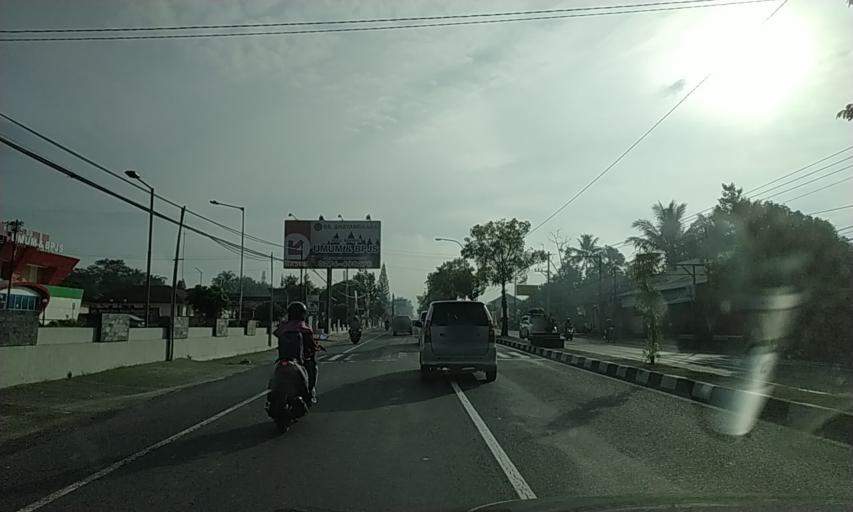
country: ID
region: Central Java
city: Candi Prambanan
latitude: -7.7667
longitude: 110.4718
